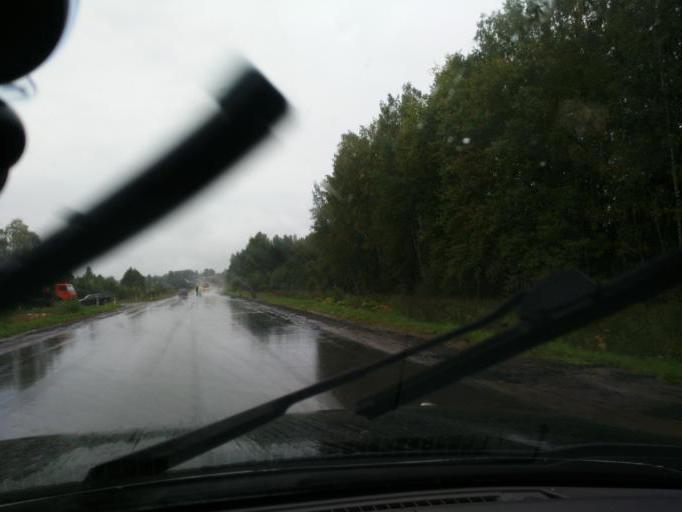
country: RU
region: Perm
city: Osa
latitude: 57.3625
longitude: 55.6027
